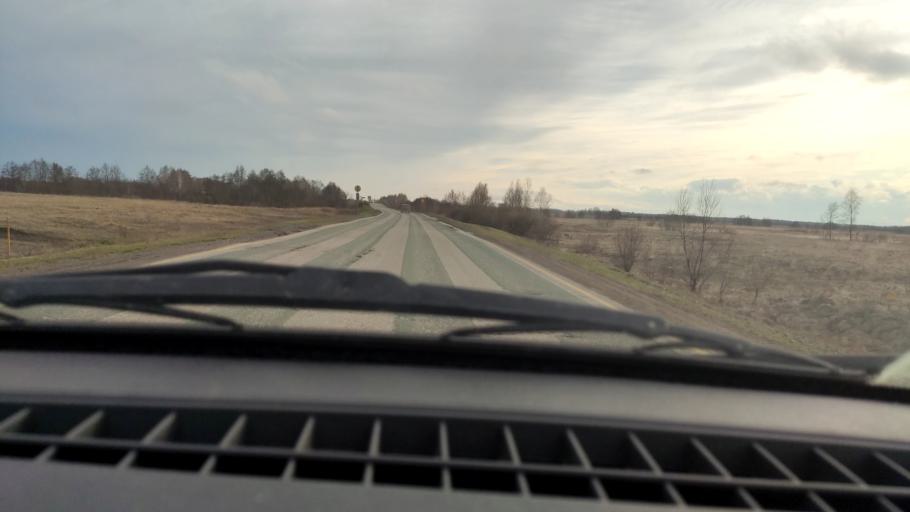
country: RU
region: Bashkortostan
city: Chishmy
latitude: 54.4450
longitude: 55.2428
